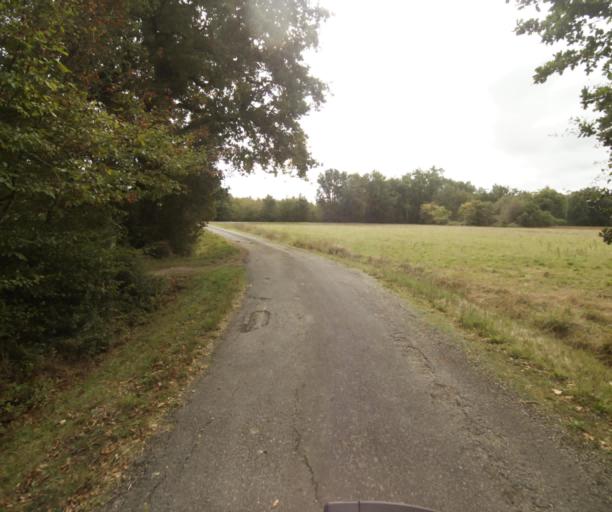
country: FR
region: Midi-Pyrenees
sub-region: Departement du Tarn-et-Garonne
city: Montech
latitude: 43.9747
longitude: 1.2524
